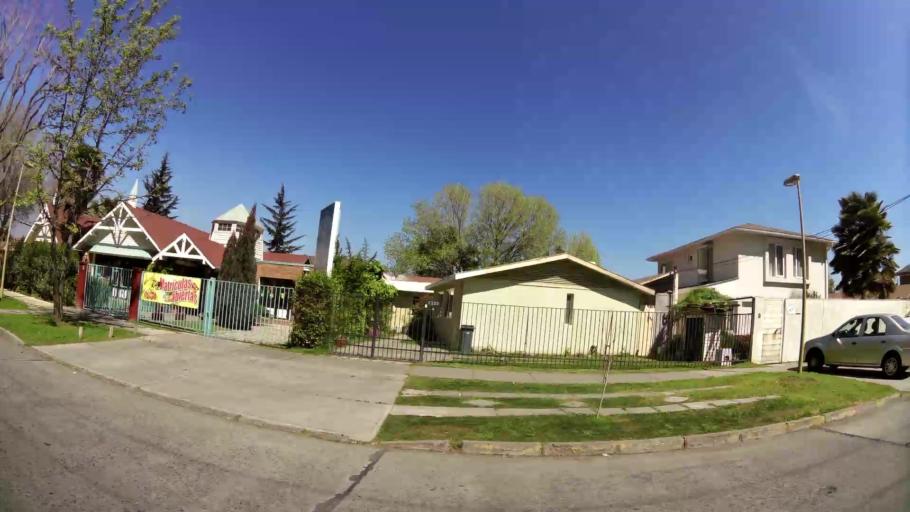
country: CL
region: Santiago Metropolitan
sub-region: Provincia de Santiago
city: Villa Presidente Frei, Nunoa, Santiago, Chile
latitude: -33.4201
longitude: -70.5554
